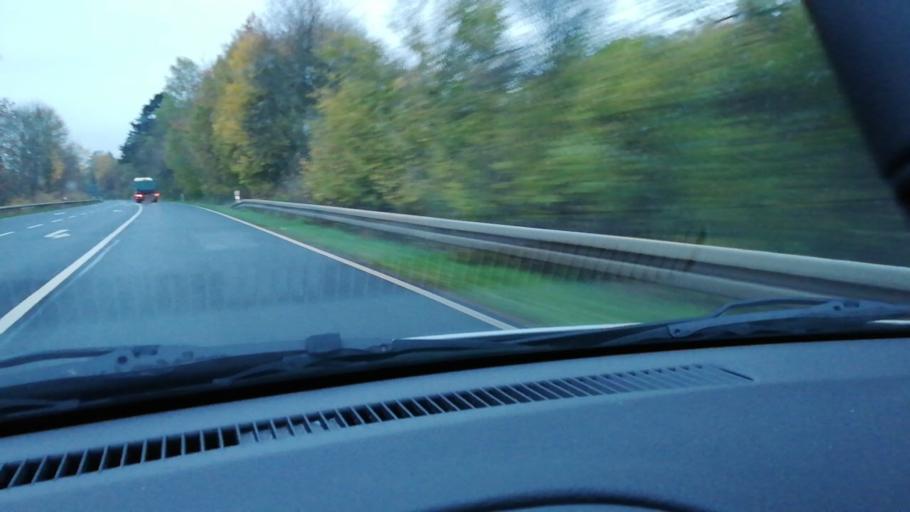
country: DE
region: Bavaria
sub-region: Regierungsbezirk Unterfranken
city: Hosbach
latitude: 50.0301
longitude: 9.2104
